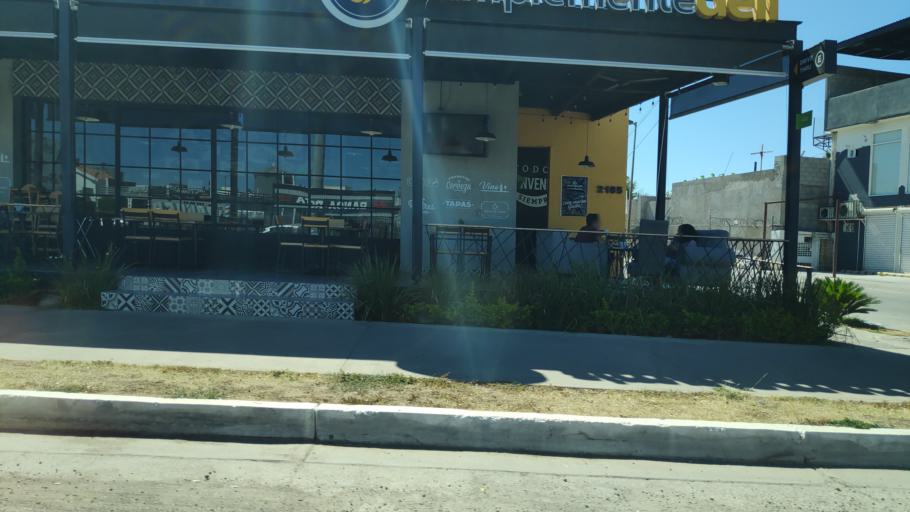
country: MX
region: Sinaloa
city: Culiacan
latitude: 24.8294
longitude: -107.3996
